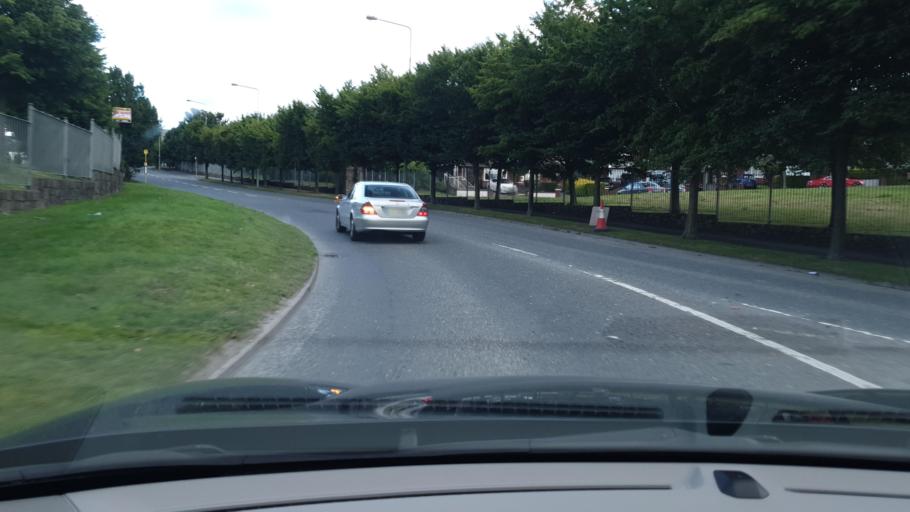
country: IE
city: Jobstown
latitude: 53.2781
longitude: -6.4199
